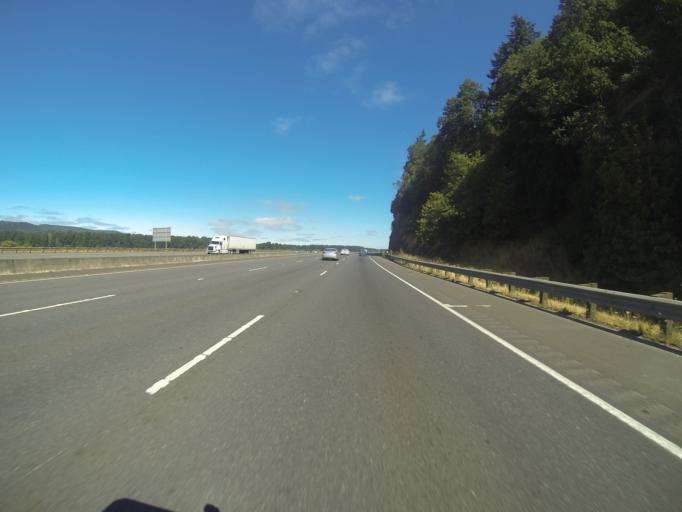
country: US
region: Washington
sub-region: Cowlitz County
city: Kalama
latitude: 46.0595
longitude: -122.8659
